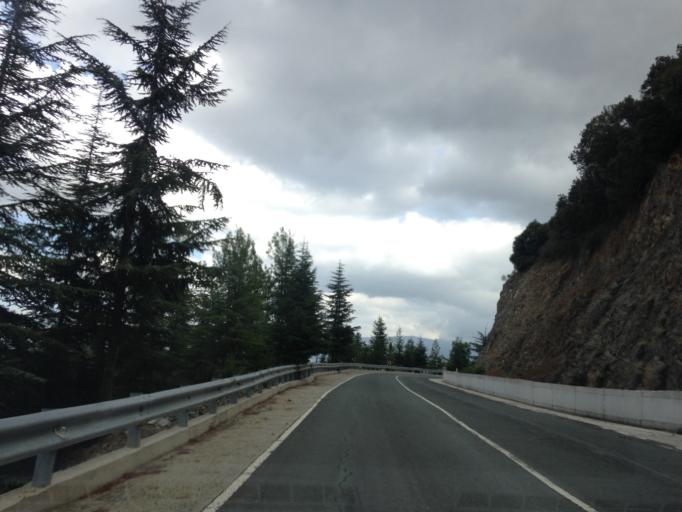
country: CY
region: Lefkosia
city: Lefka
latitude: 34.9937
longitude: 32.7363
